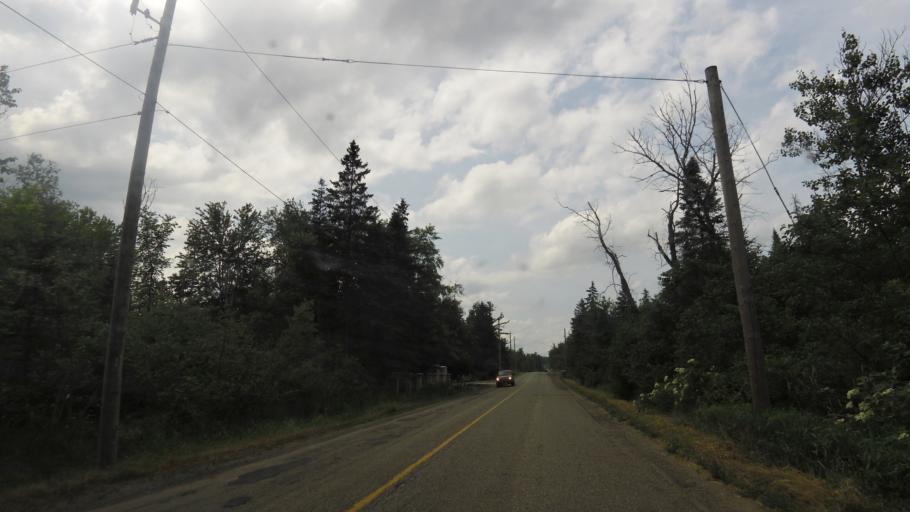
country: CA
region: Ontario
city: Brampton
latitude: 43.8459
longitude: -79.8808
